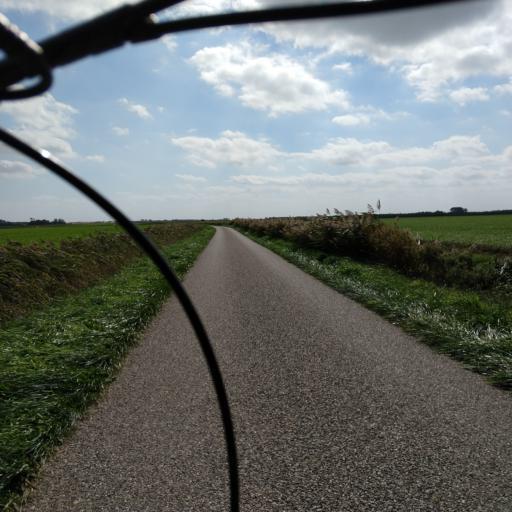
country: NL
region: Zeeland
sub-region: Gemeente Noord-Beveland
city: Kamperland
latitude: 51.5942
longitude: 3.7617
